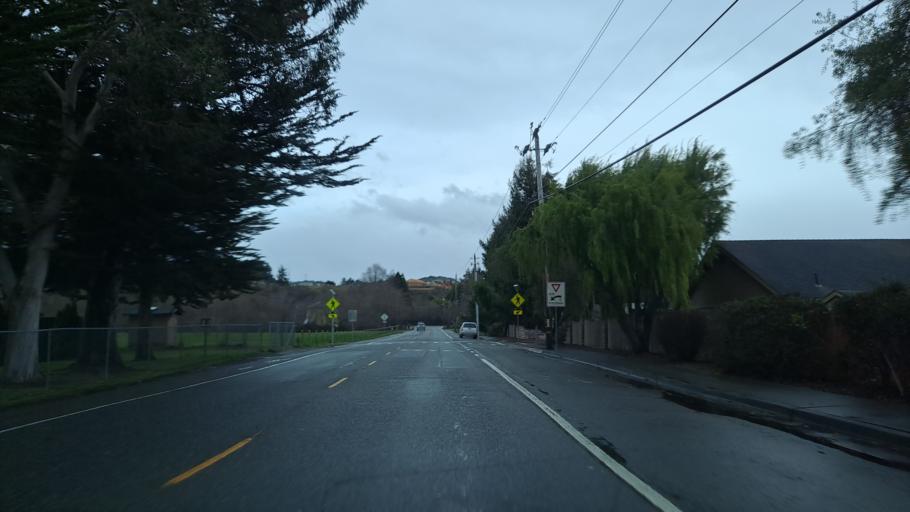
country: US
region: California
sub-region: Humboldt County
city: Fortuna
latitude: 40.5908
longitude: -124.1364
